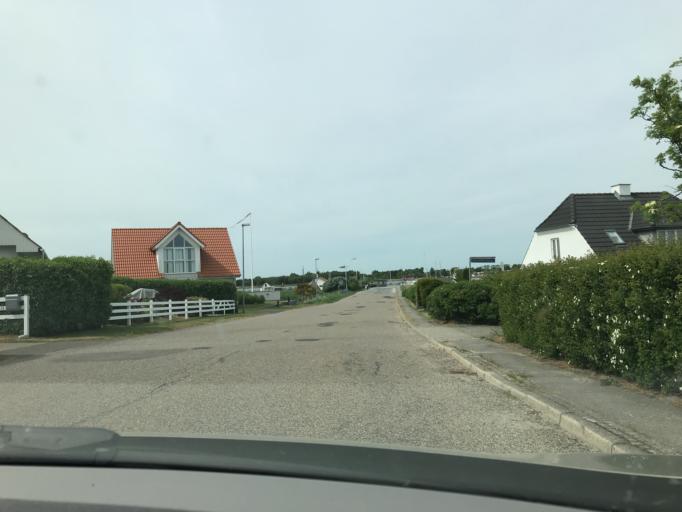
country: DK
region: Central Jutland
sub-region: Norddjurs Kommune
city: Allingabro
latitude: 56.6045
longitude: 10.3044
